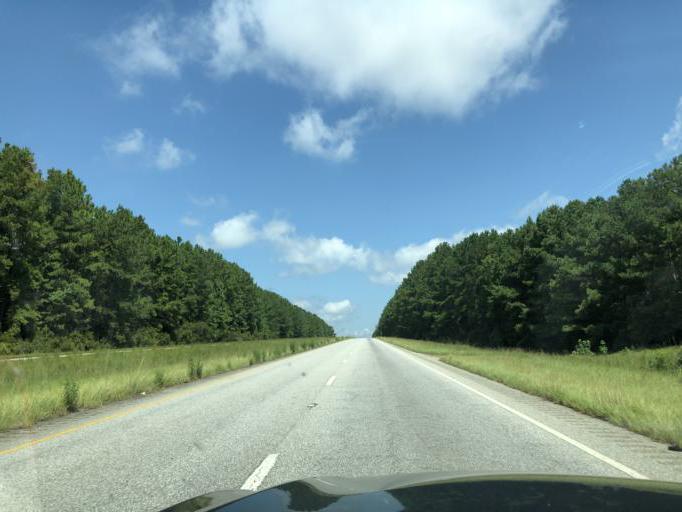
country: US
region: Alabama
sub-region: Henry County
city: Abbeville
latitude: 31.6822
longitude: -85.2790
